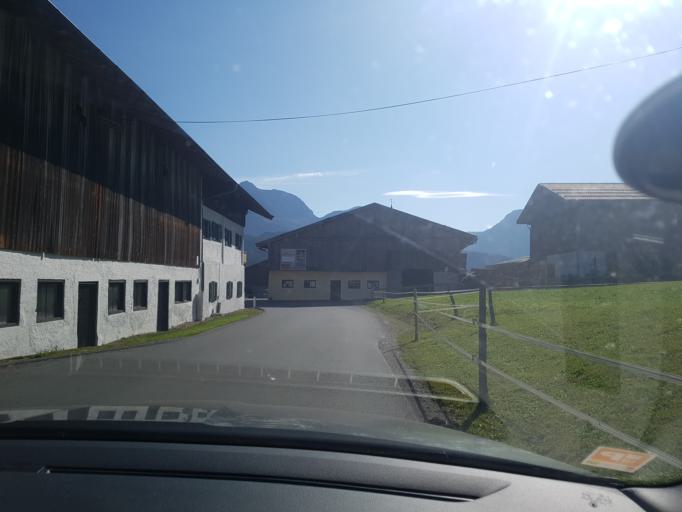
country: AT
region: Tyrol
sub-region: Politischer Bezirk Kitzbuhel
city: Hochfilzen
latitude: 47.4818
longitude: 12.6120
